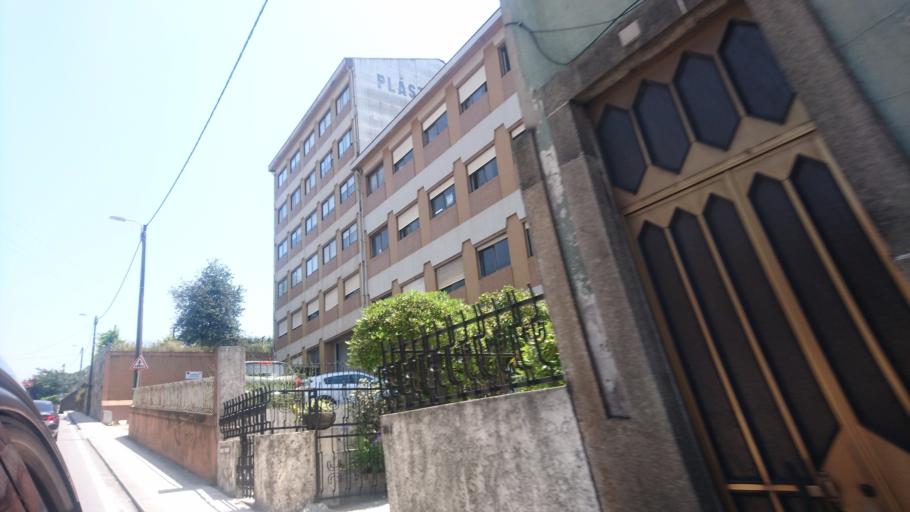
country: PT
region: Porto
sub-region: Gondomar
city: Rio Tinto
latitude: 41.1680
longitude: -8.5623
